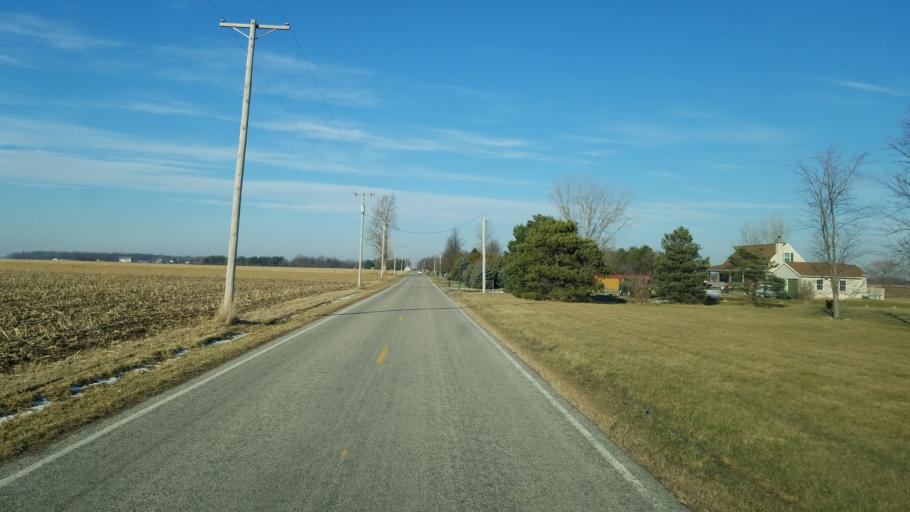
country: US
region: Ohio
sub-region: Sandusky County
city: Mount Carmel
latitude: 41.3010
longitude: -82.9027
